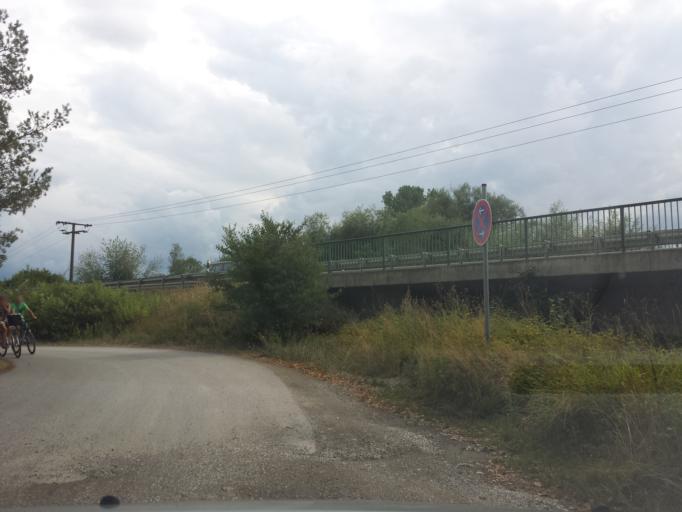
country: DE
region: Bavaria
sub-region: Swabia
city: Rettenbach
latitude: 48.4554
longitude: 10.3801
